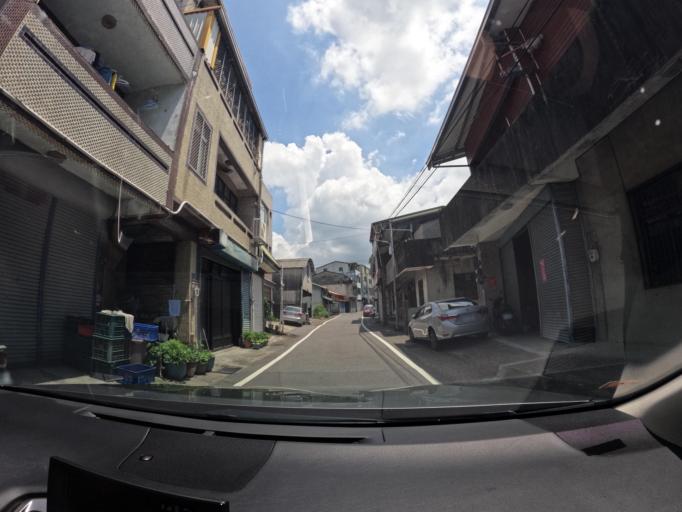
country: TW
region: Taiwan
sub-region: Miaoli
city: Miaoli
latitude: 24.4127
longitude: 120.7780
